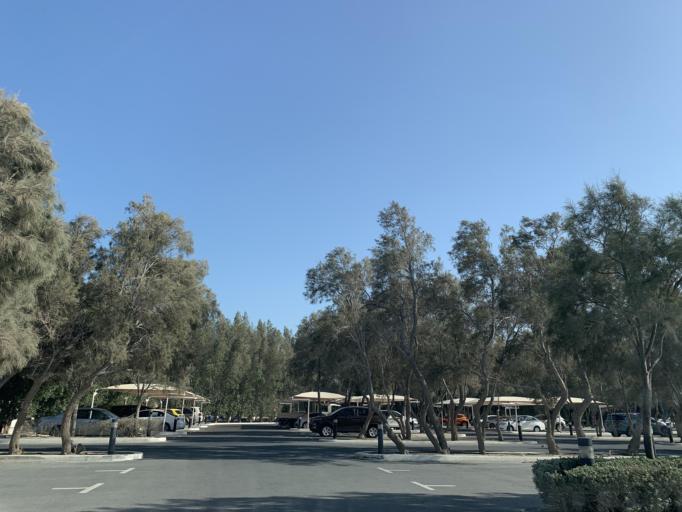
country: BH
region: Muharraq
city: Al Muharraq
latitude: 26.2425
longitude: 50.5968
